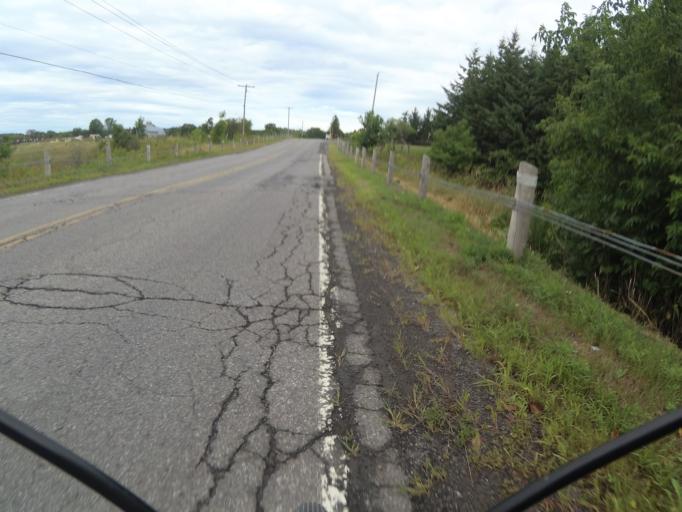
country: CA
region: Ontario
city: Bourget
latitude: 45.3888
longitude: -75.2777
